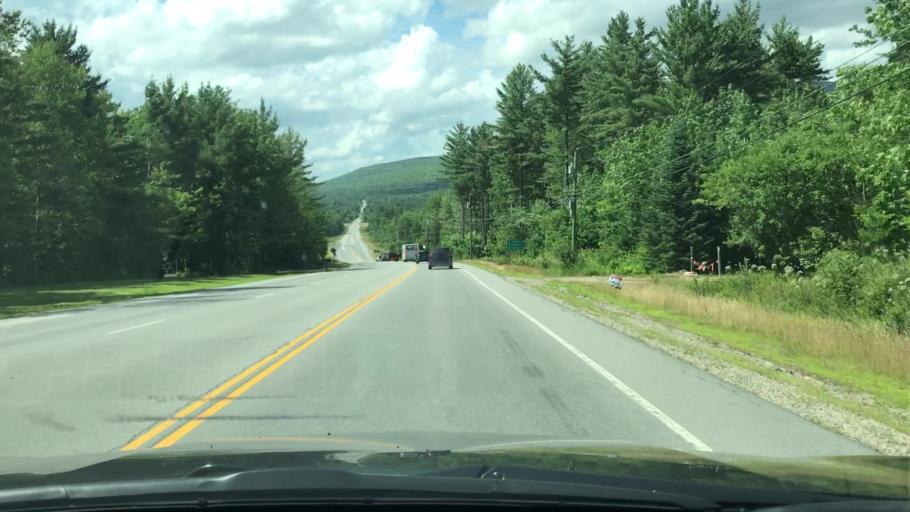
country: US
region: New Hampshire
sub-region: Coos County
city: Jefferson
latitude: 44.3775
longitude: -71.4133
